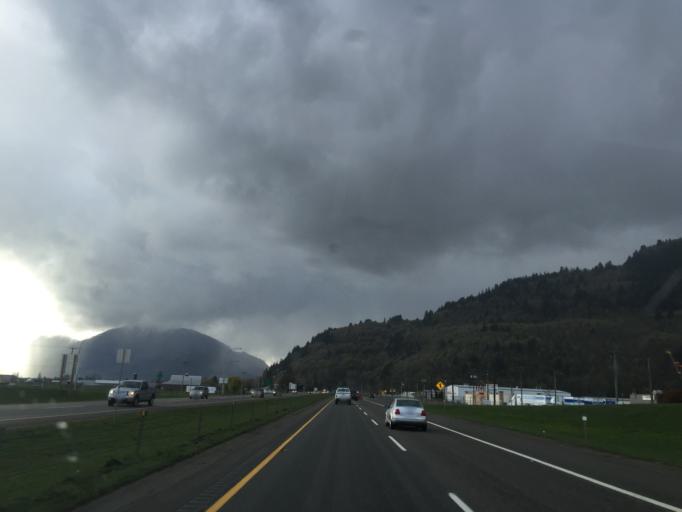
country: CA
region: British Columbia
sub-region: Fraser Valley Regional District
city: Chilliwack
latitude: 49.1444
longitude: -122.0074
